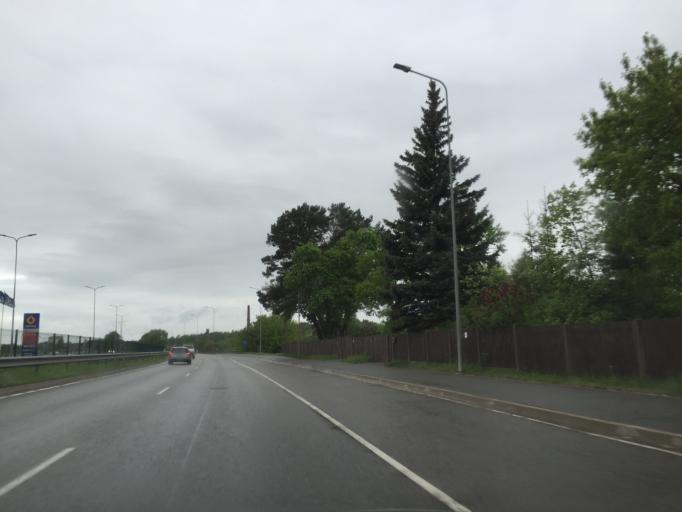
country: LV
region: Ogre
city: Ogre
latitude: 56.8161
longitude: 24.5896
